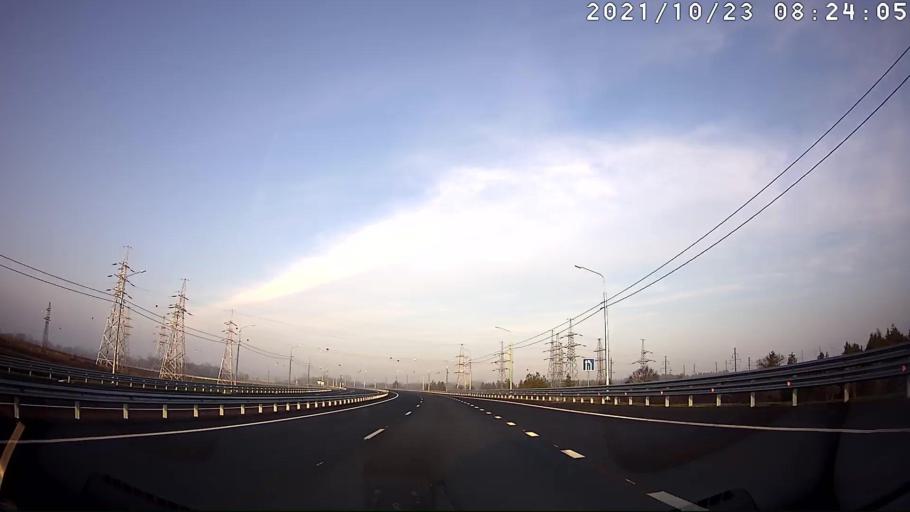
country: RU
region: Saratov
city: Sennoy
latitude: 52.1441
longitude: 46.9123
